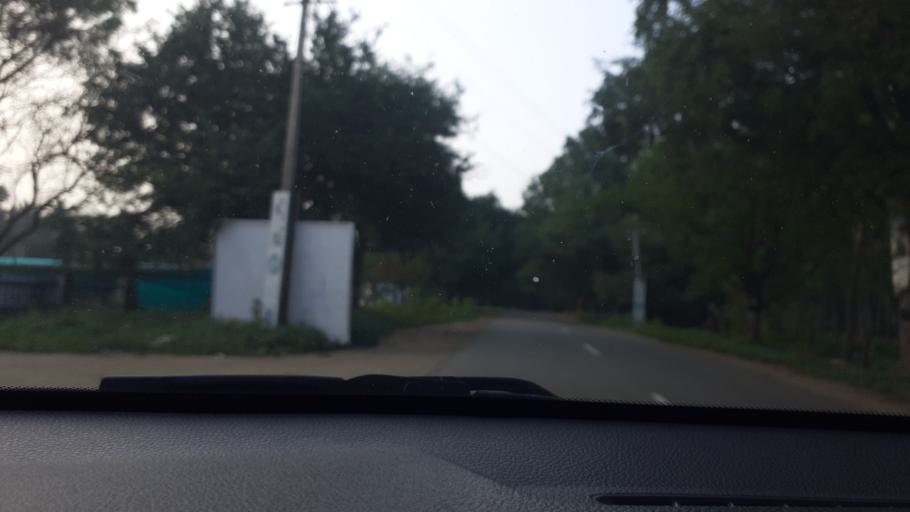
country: IN
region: Tamil Nadu
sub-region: Dindigul
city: Palani
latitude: 10.4277
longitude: 77.5314
